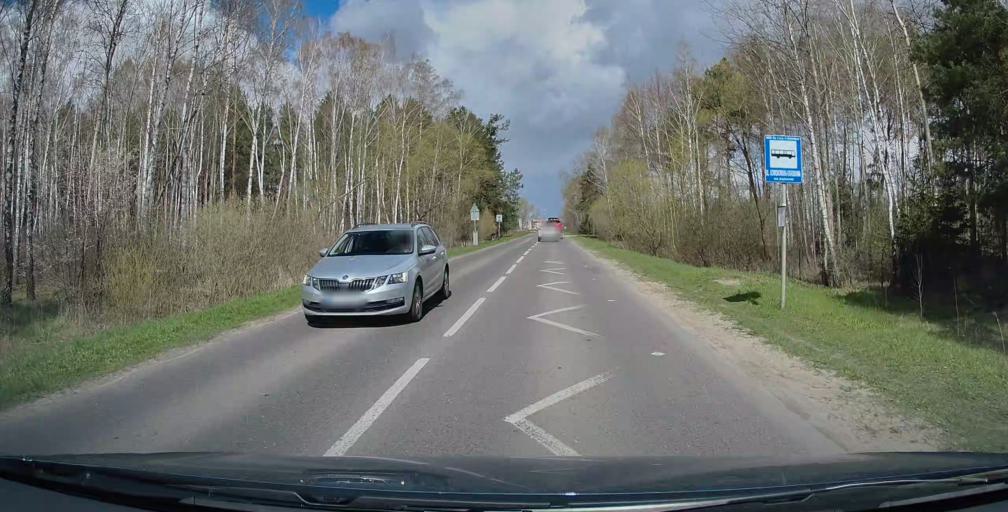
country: PL
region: Masovian Voivodeship
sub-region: Ostroleka
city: Ostroleka
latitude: 53.0573
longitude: 21.5855
